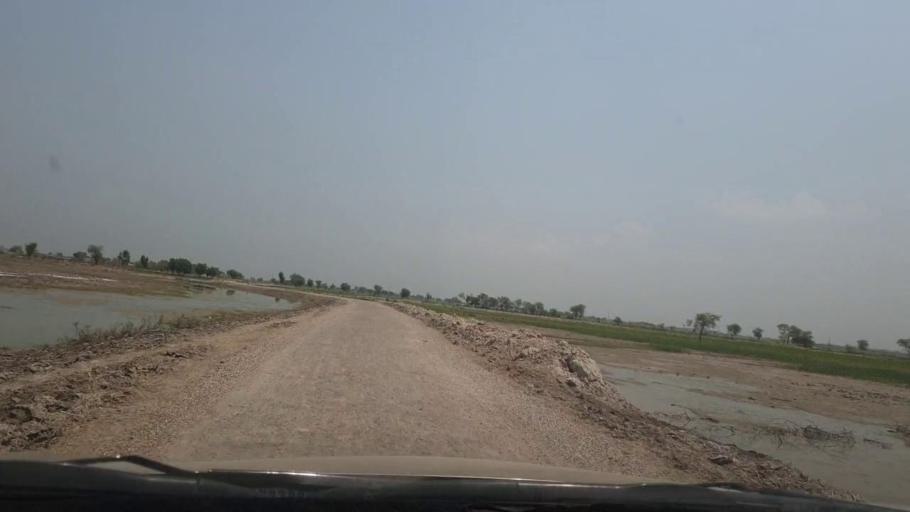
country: PK
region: Sindh
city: Ratodero
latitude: 27.7225
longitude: 68.2895
